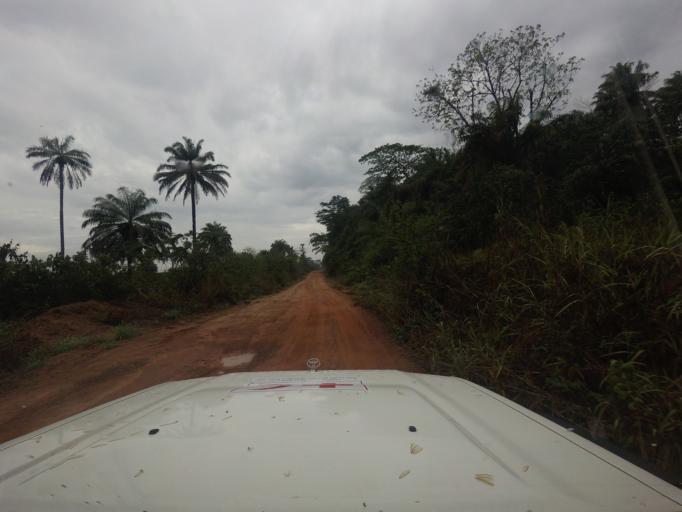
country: LR
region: Lofa
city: Voinjama
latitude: 8.3750
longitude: -9.8593
